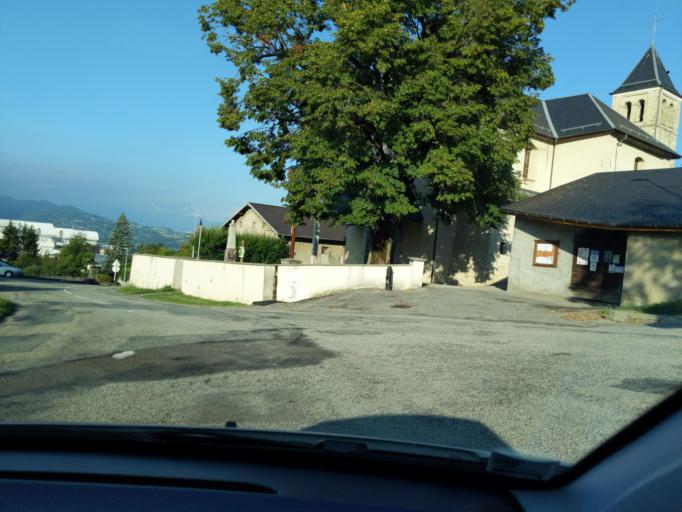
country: FR
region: Rhone-Alpes
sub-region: Departement de la Savoie
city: Aiton
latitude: 45.5609
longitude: 6.2575
